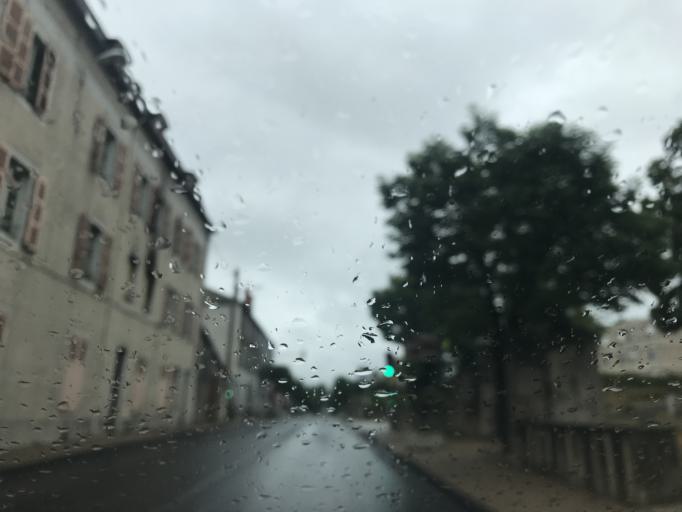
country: FR
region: Auvergne
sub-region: Departement du Puy-de-Dome
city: Ambert
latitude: 45.5525
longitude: 3.7399
